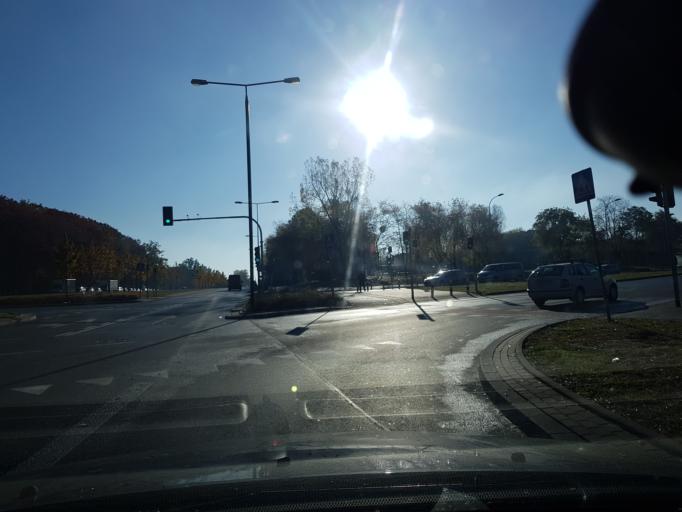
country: PL
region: Masovian Voivodeship
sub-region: Warszawa
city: Bielany
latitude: 52.2856
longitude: 20.9405
